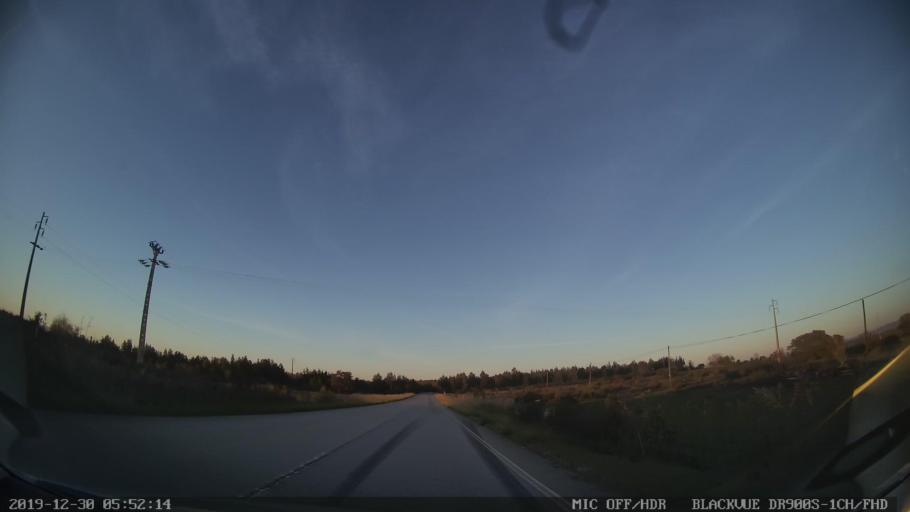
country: PT
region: Castelo Branco
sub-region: Idanha-A-Nova
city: Idanha-a-Nova
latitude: 40.0034
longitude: -7.2485
